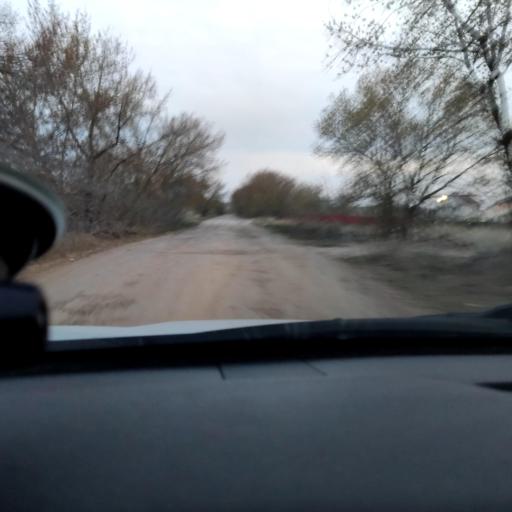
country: RU
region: Samara
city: Smyshlyayevka
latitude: 53.1536
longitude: 50.3916
